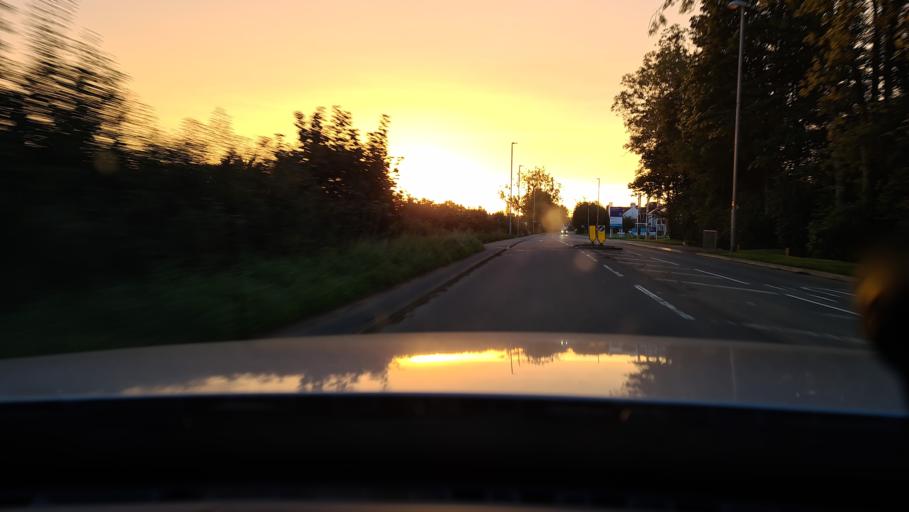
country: GB
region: England
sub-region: Leicestershire
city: Sapcote
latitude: 52.5378
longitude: -1.2909
